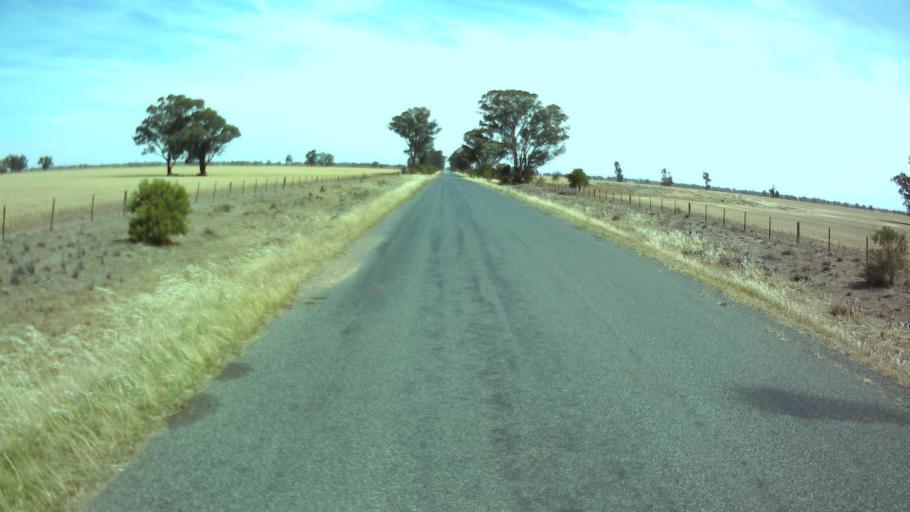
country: AU
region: New South Wales
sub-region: Weddin
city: Grenfell
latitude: -33.9675
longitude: 147.7805
